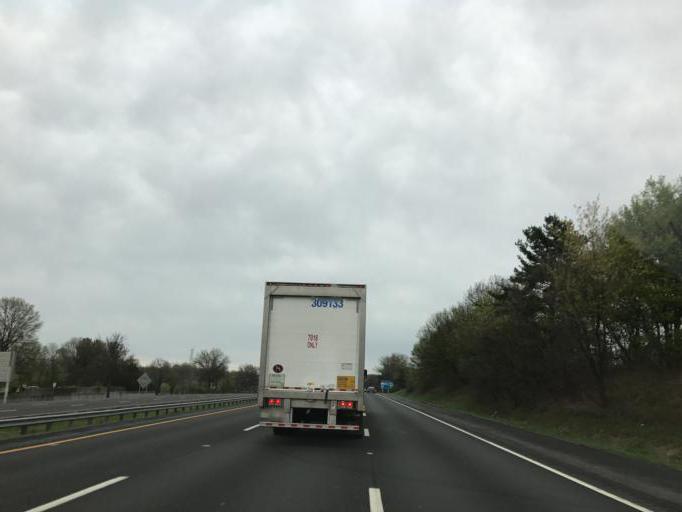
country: US
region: New Jersey
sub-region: Hunterdon County
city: Glen Gardner
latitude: 40.6395
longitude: -74.9855
